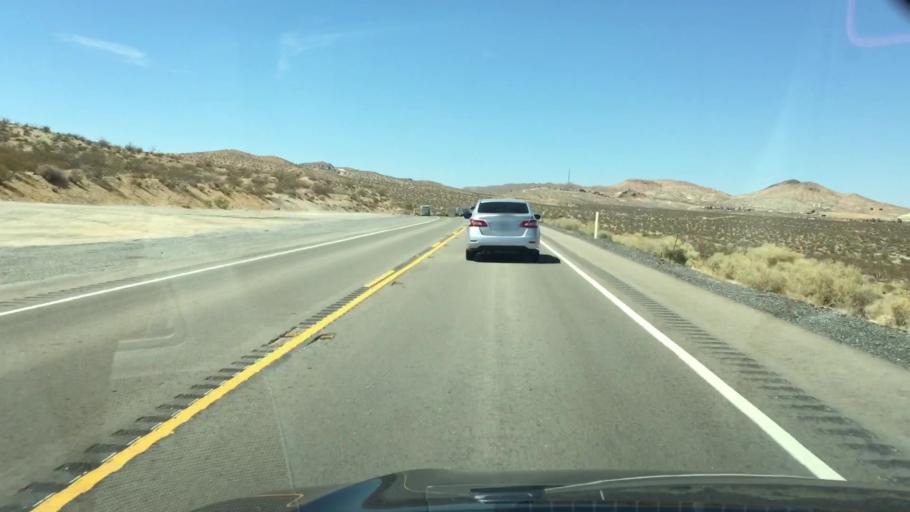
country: US
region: California
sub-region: Kern County
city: Ridgecrest
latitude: 35.3253
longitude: -117.6132
